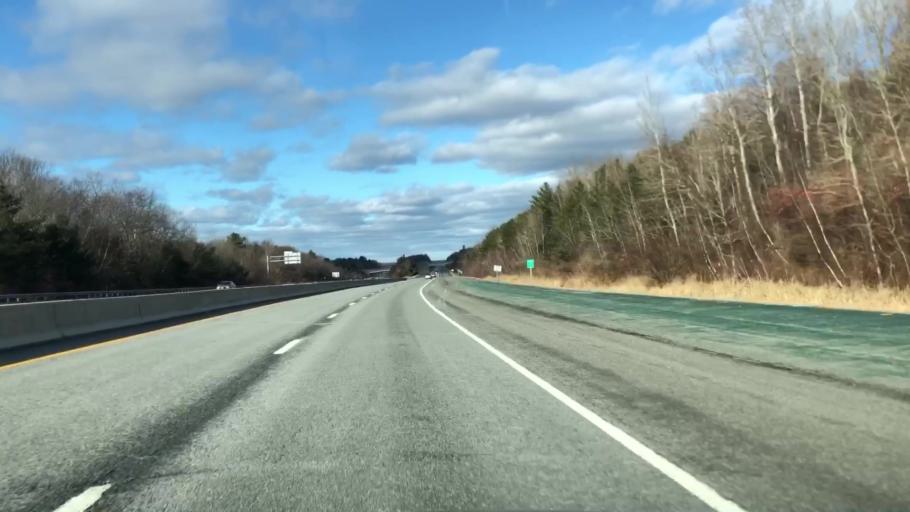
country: US
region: Massachusetts
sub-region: Worcester County
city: West Boylston
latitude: 42.3513
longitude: -71.8103
